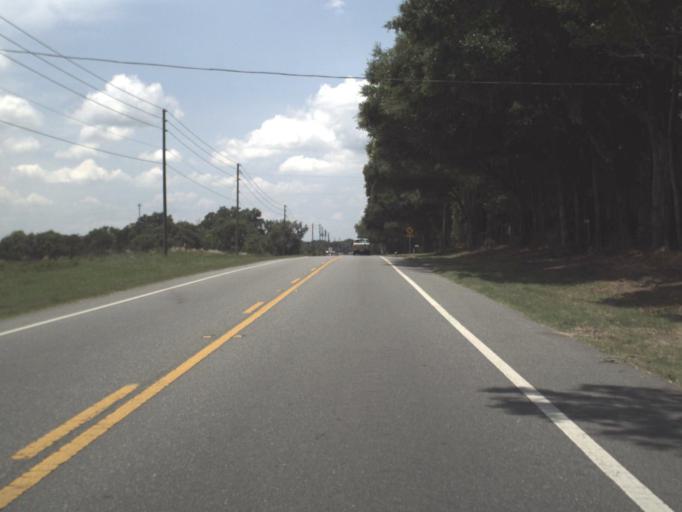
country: US
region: Florida
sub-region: Alachua County
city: Newberry
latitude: 29.6442
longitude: -82.6522
